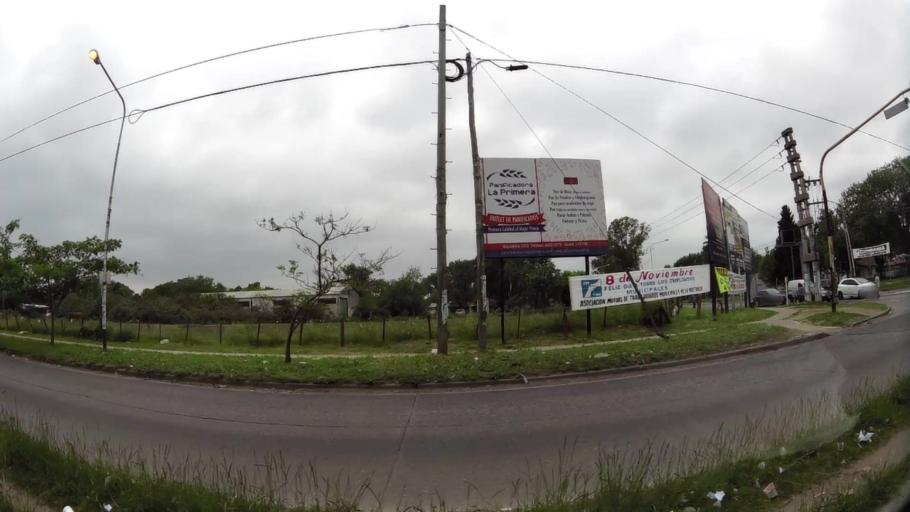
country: AR
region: Buenos Aires
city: San Justo
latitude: -34.7293
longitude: -58.5264
